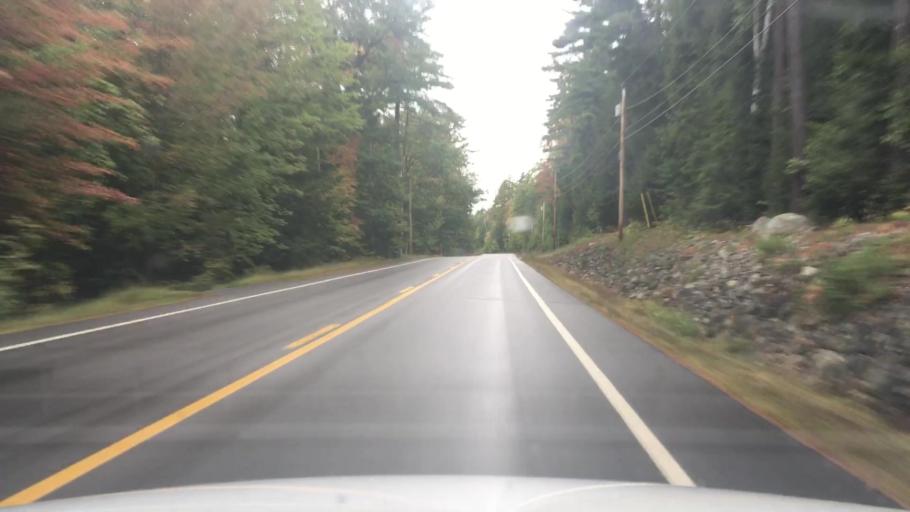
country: US
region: Maine
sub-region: Kennebec County
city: Rome
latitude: 44.5420
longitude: -69.8916
